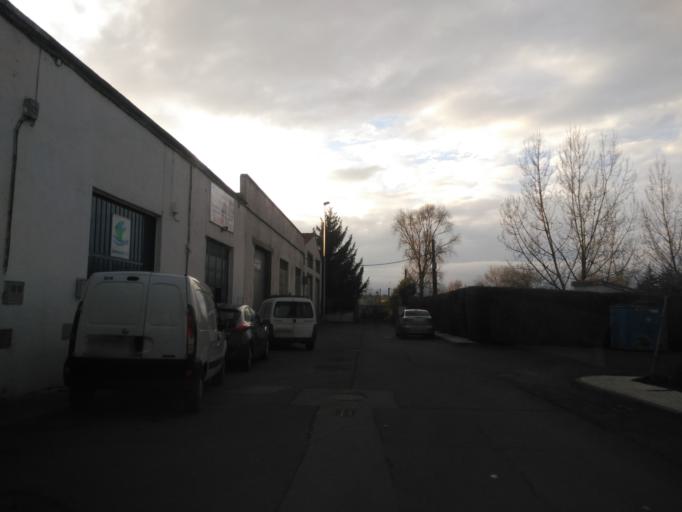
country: ES
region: Castille and Leon
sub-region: Provincia de Salamanca
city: Santa Marta de Tormes
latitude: 40.9478
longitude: -5.6386
